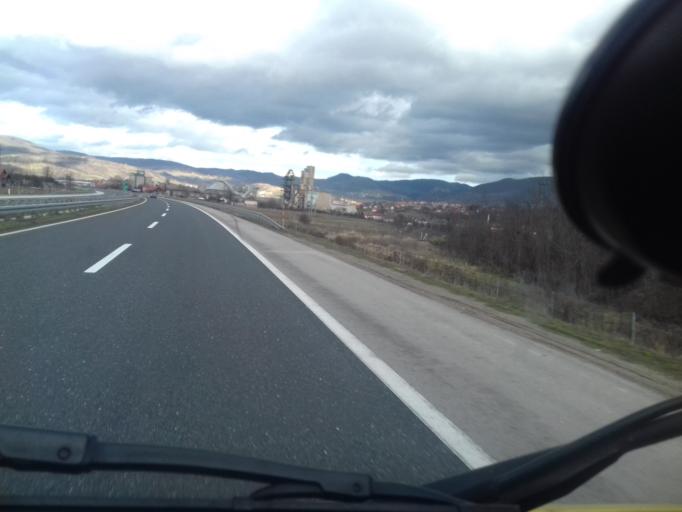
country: BA
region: Federation of Bosnia and Herzegovina
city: Kakanj
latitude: 44.1076
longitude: 18.1116
